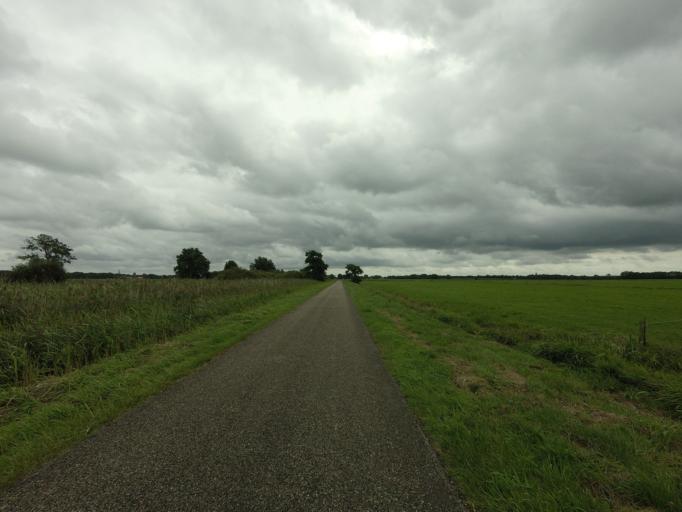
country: NL
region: Friesland
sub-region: Gemeente Weststellingwerf
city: Steggerda
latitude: 52.8647
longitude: 6.0626
